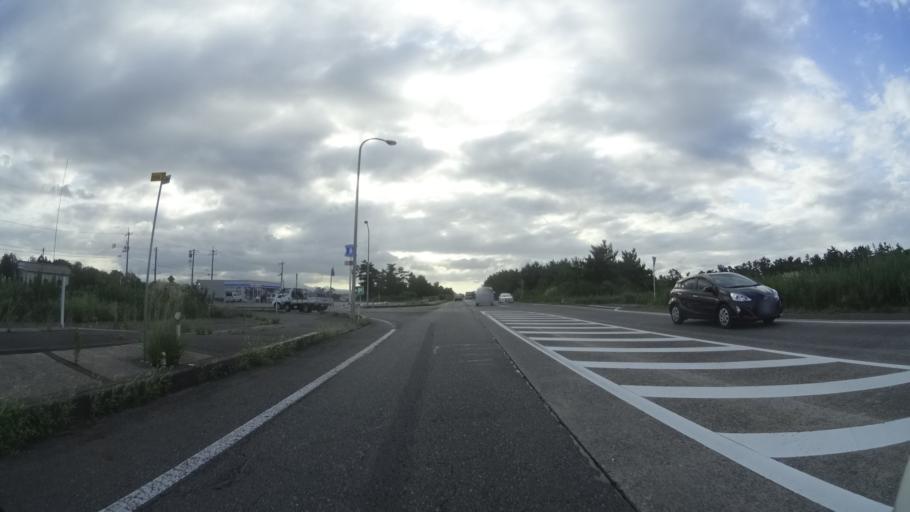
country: JP
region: Tottori
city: Kurayoshi
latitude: 35.4984
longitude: 133.7883
